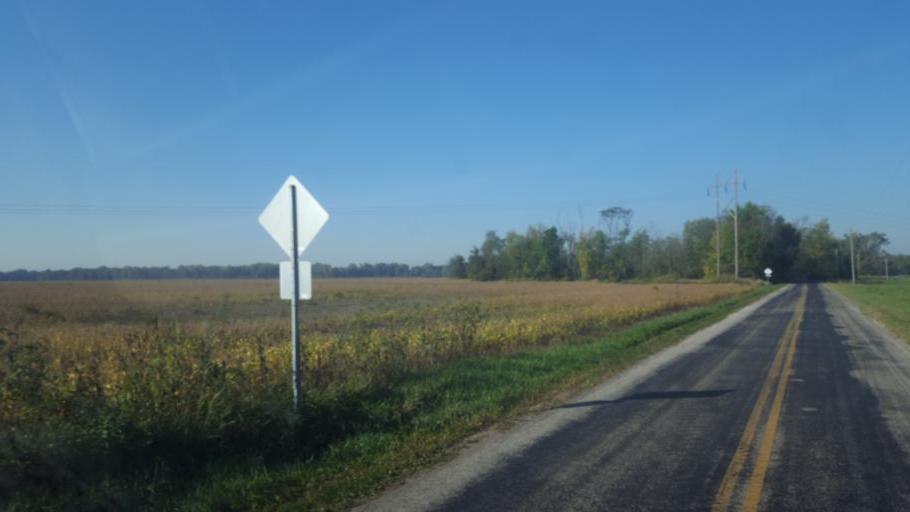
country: US
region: Ohio
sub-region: Union County
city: Richwood
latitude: 40.5475
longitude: -83.3370
